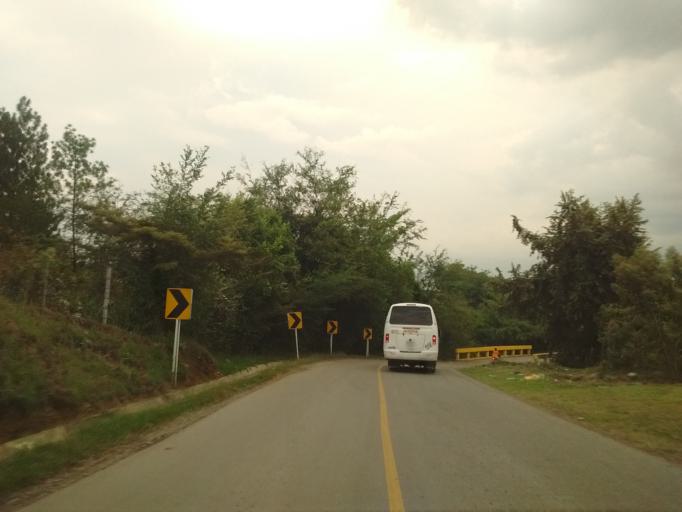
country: CO
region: Cauca
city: Caloto
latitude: 3.0589
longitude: -76.3720
